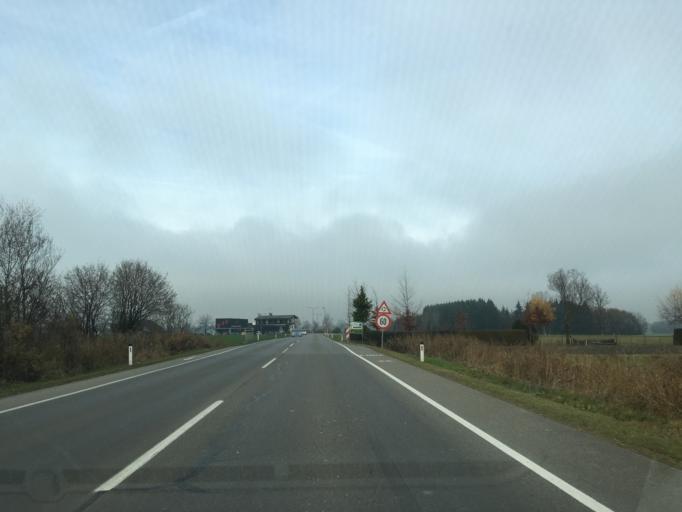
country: CH
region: Saint Gallen
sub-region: Wahlkreis Rheintal
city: Diepoldsau
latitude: 47.3960
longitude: 9.6797
